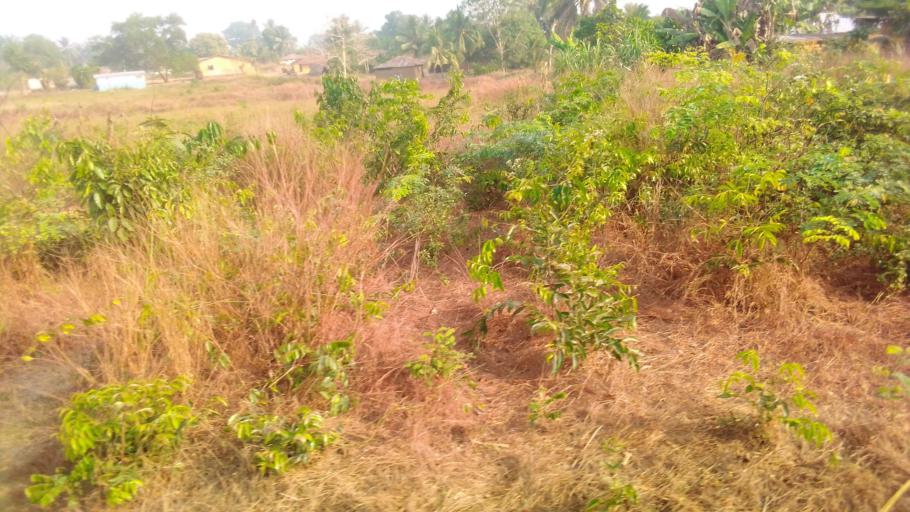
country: SL
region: Southern Province
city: Sumbuya
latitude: 7.6007
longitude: -12.1664
